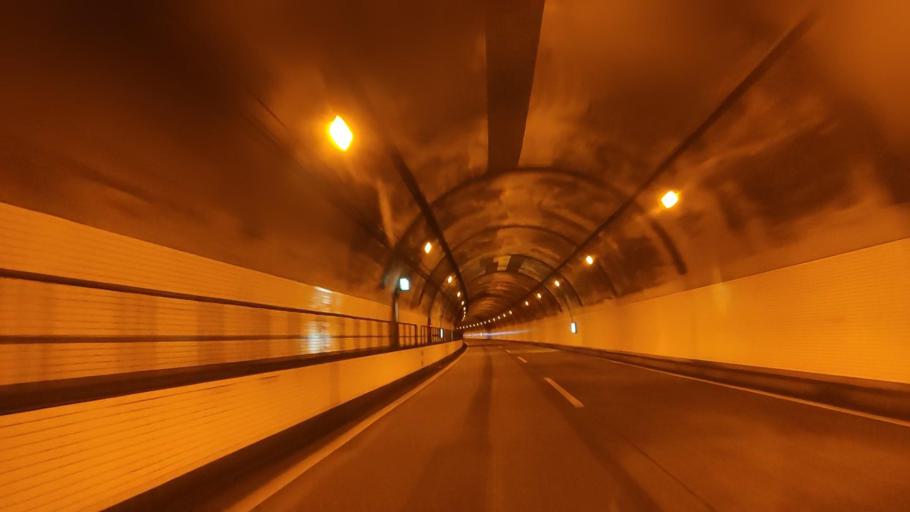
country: JP
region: Niigata
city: Itoigawa
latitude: 37.0178
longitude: 137.8348
